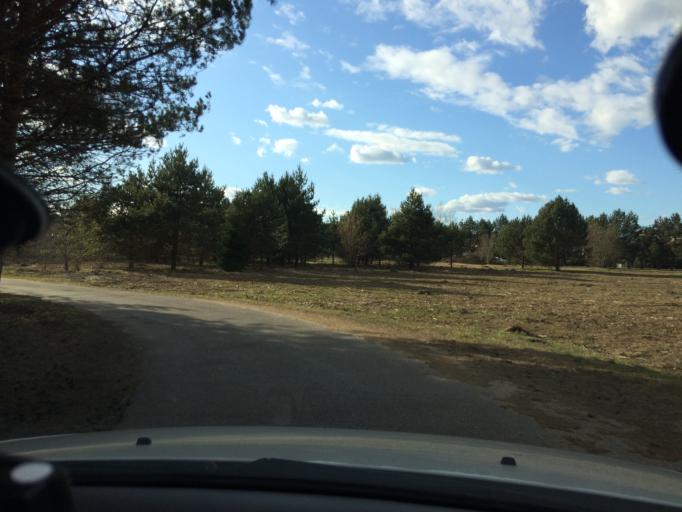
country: LT
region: Vilnius County
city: Rasos
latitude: 54.7772
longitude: 25.3474
